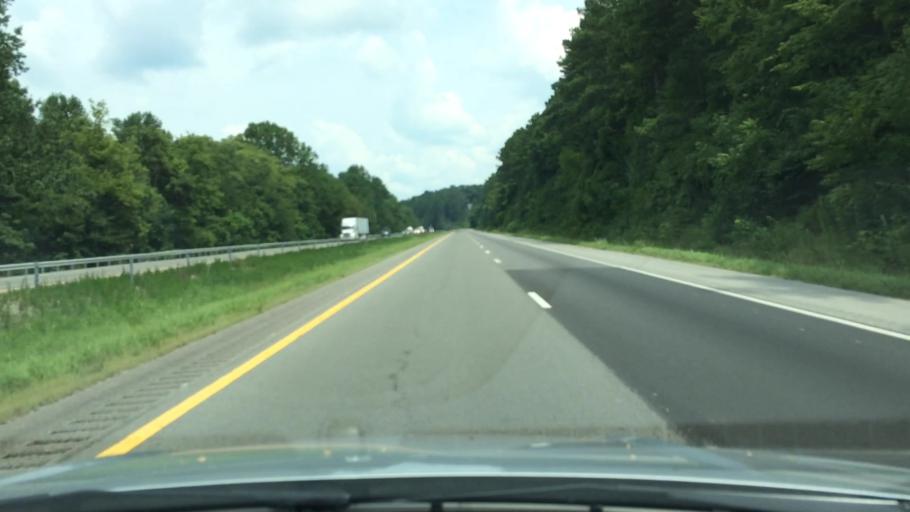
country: US
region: Tennessee
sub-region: Marshall County
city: Cornersville
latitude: 35.2539
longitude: -86.8828
